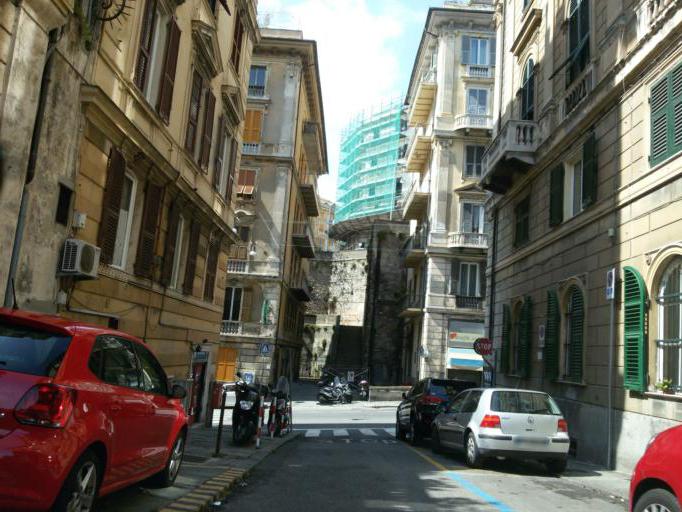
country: IT
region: Liguria
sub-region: Provincia di Genova
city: Genoa
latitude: 44.4124
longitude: 8.9444
